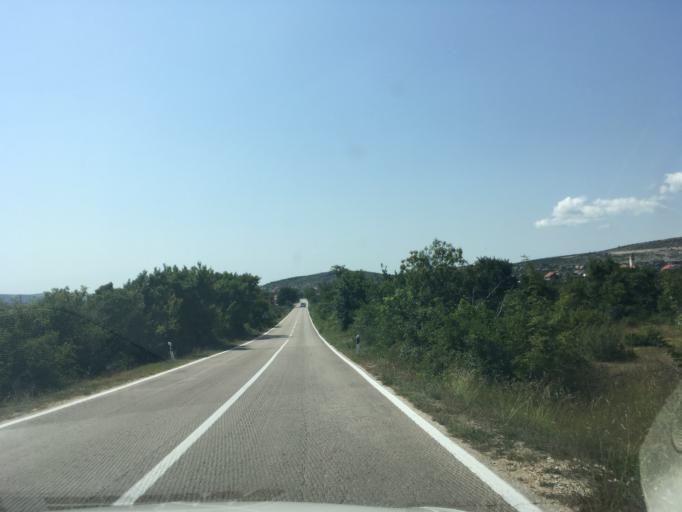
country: HR
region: Sibensko-Kniniska
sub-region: Grad Sibenik
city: Pirovac
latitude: 43.9595
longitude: 15.7718
